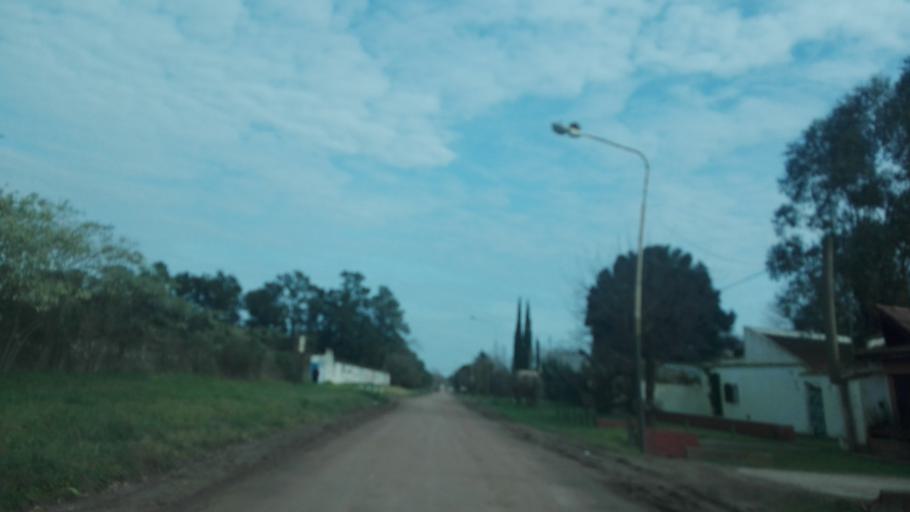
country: AR
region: Buenos Aires
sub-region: Partido de Chascomus
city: Chascomus
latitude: -35.5826
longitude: -57.9925
